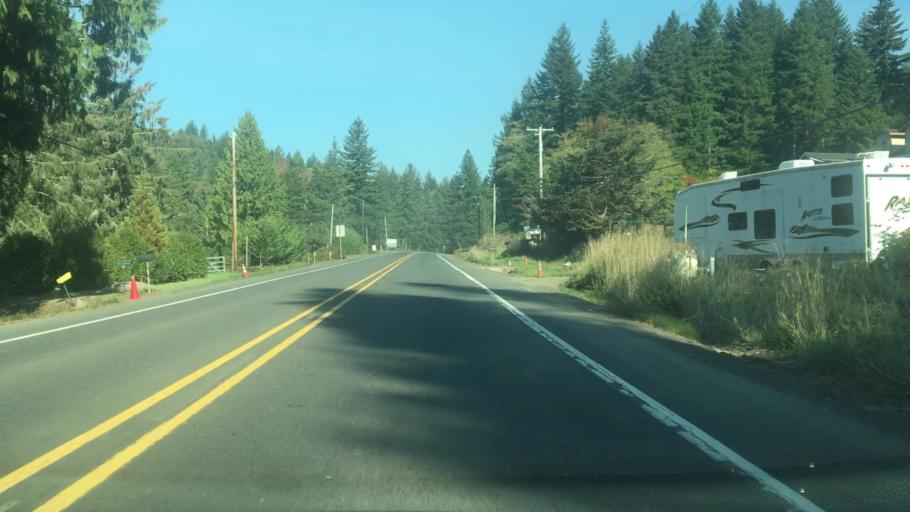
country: US
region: Oregon
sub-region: Lincoln County
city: Rose Lodge
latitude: 45.0164
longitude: -123.8715
